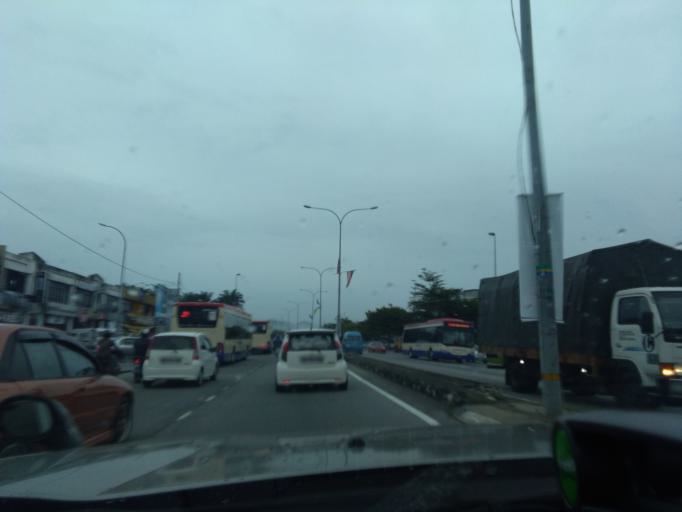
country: MY
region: Penang
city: Nibong Tebal
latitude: 5.1797
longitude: 100.4834
